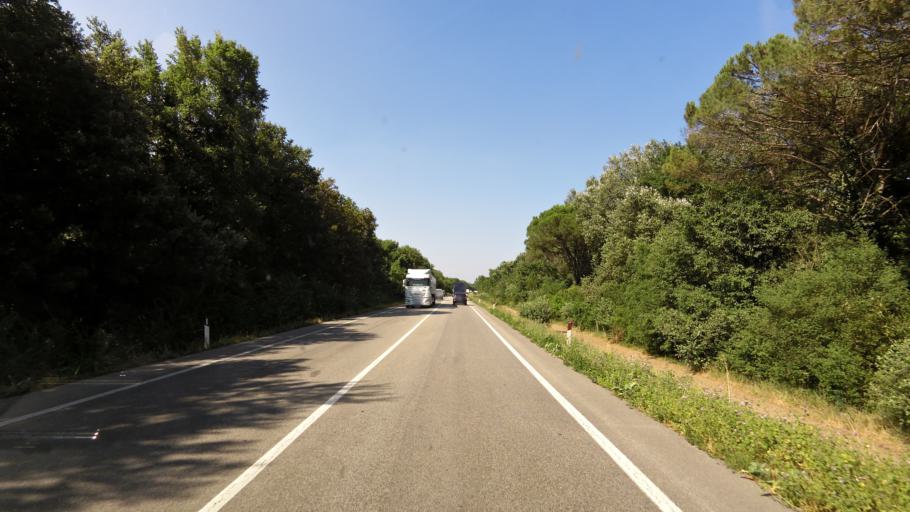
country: IT
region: Emilia-Romagna
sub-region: Provincia di Ravenna
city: Marina Romea
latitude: 44.4951
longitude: 12.2163
